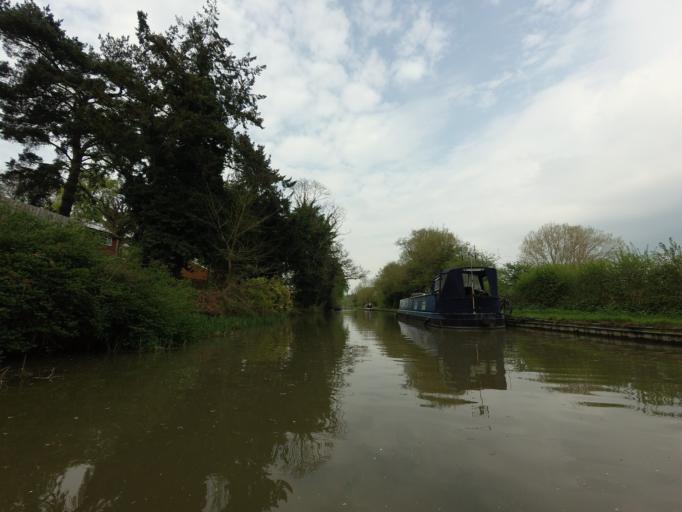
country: GB
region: England
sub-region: Central Bedfordshire
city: Leighton Buzzard
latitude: 51.9249
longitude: -0.6662
